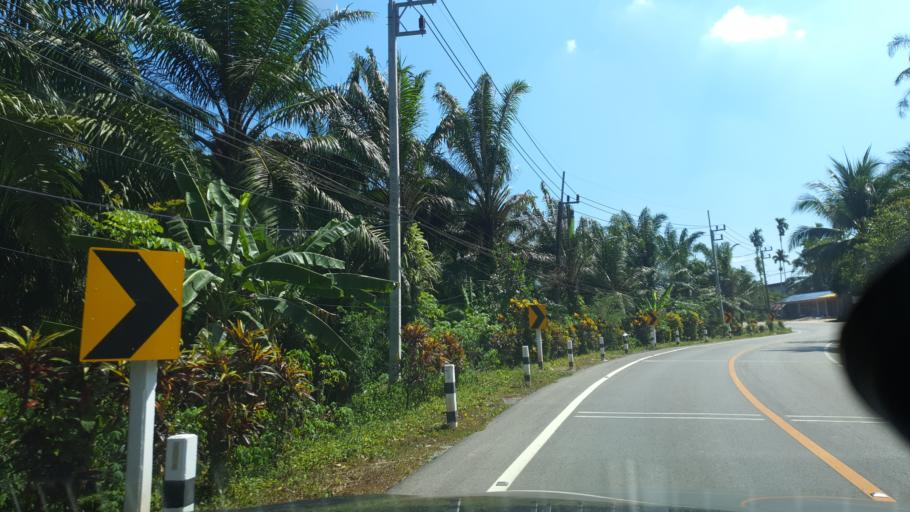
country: TH
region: Krabi
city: Khlong Thom
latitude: 7.9232
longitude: 99.2446
